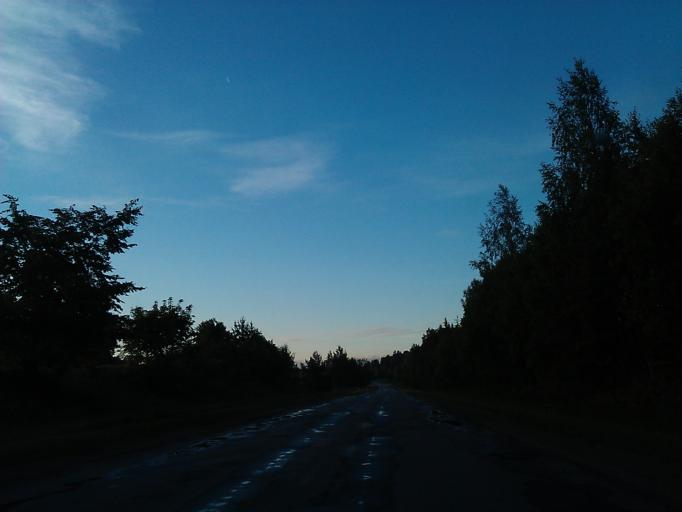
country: LV
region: Pargaujas
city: Stalbe
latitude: 57.3499
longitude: 25.1026
